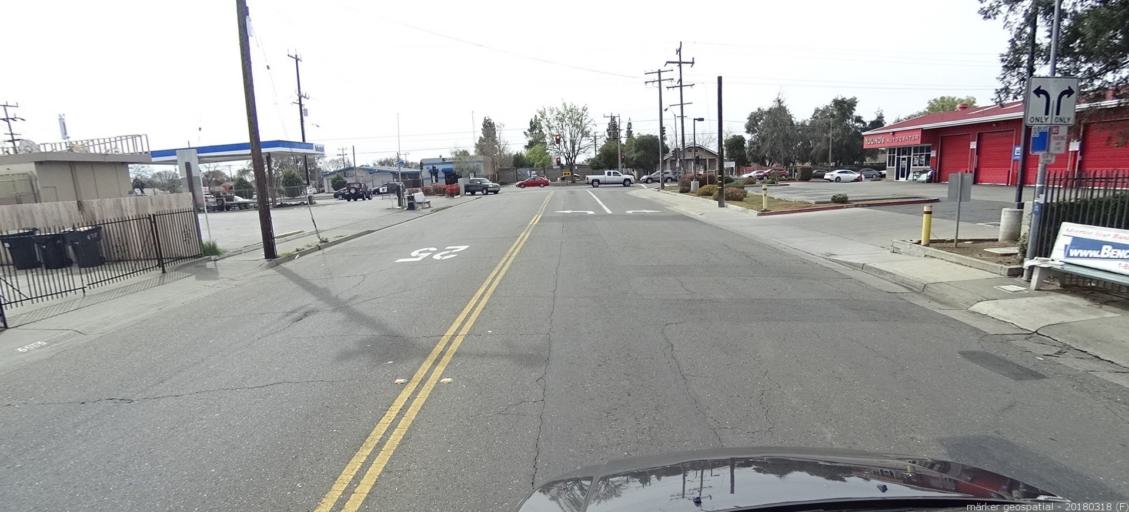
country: US
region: California
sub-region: Sacramento County
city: Parkway
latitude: 38.5255
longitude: -121.4563
